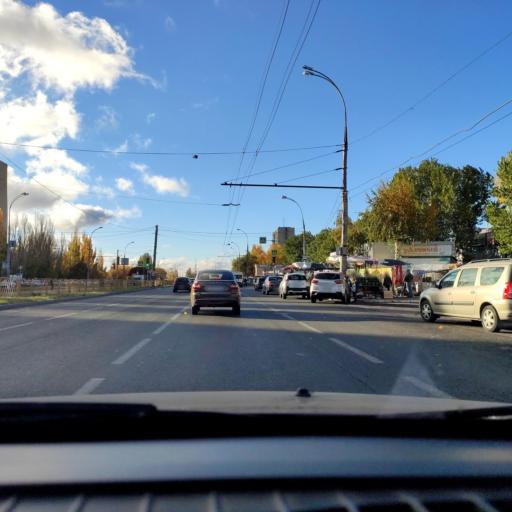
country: RU
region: Samara
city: Tol'yatti
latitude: 53.5091
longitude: 49.2923
